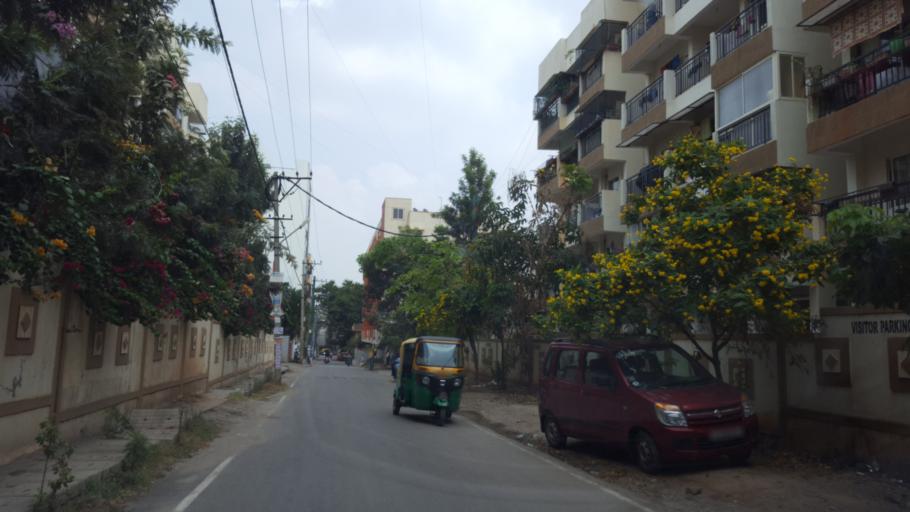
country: IN
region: Karnataka
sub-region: Bangalore Urban
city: Bangalore
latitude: 12.9691
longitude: 77.6715
